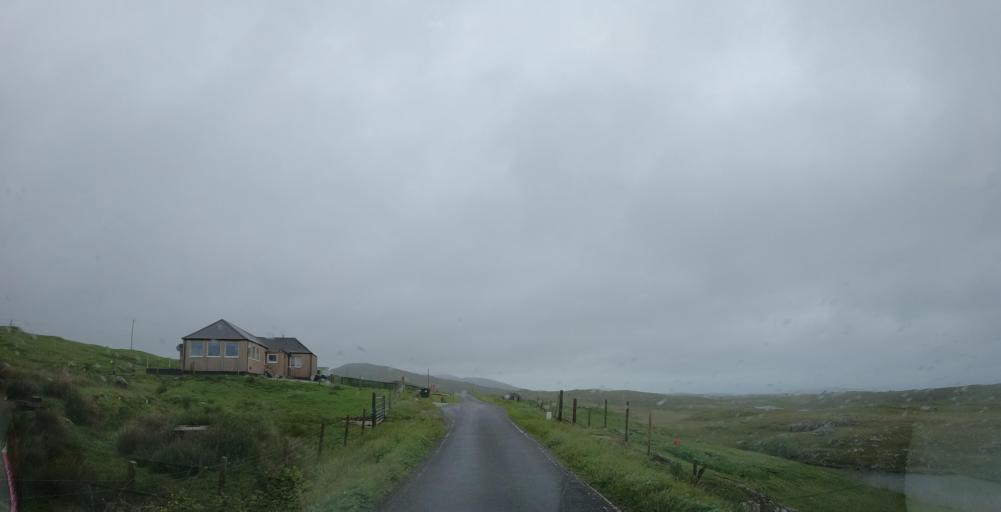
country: GB
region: Scotland
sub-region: Eilean Siar
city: Barra
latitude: 56.9861
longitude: -7.4105
